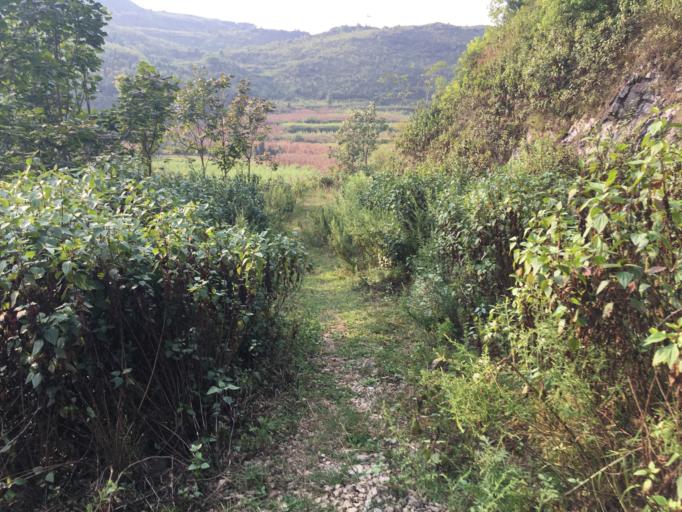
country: CN
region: Guangxi Zhuangzu Zizhiqu
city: Xinzhou
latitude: 25.4404
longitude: 105.6366
